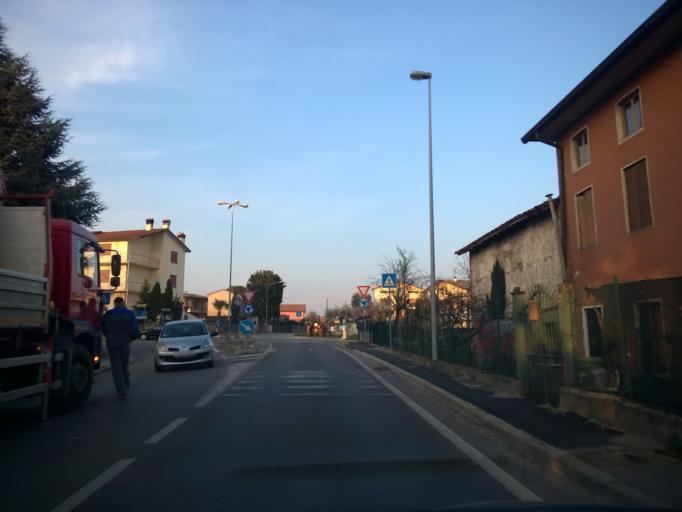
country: IT
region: Veneto
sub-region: Provincia di Vicenza
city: Caldogno-Rettorgole-Cresole
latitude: 45.6209
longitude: 11.5086
